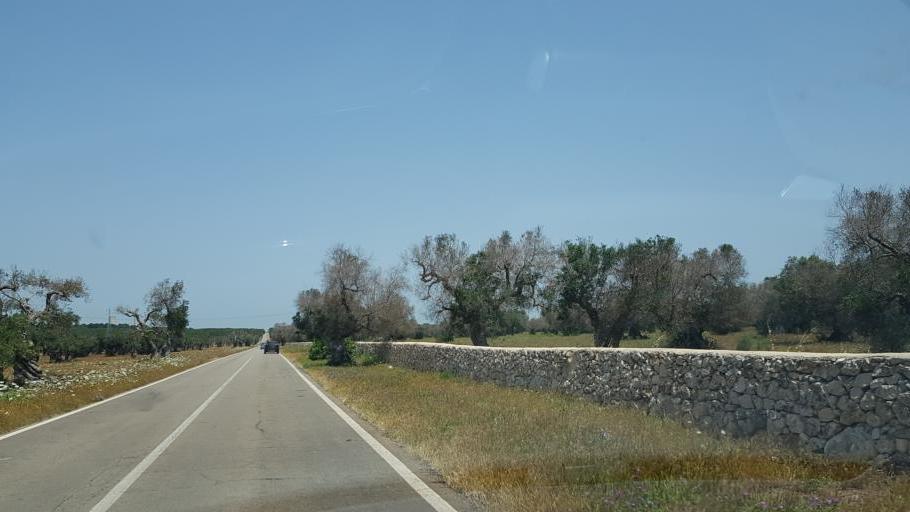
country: IT
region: Apulia
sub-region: Provincia di Lecce
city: Porto Cesareo
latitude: 40.2848
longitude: 17.9092
